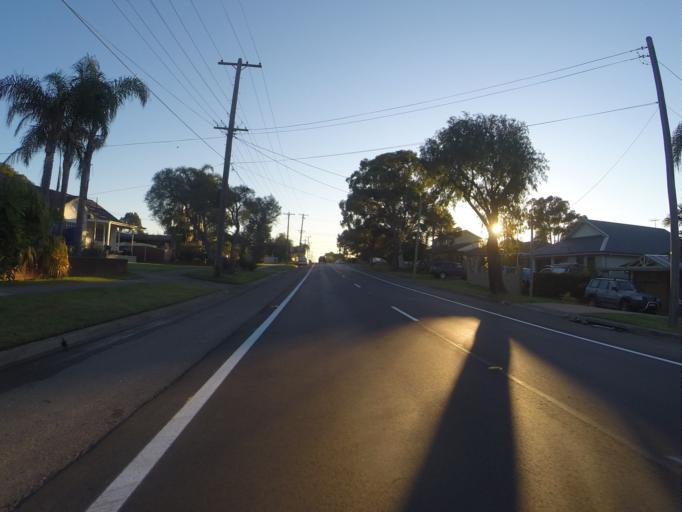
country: AU
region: New South Wales
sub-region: Sutherland Shire
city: Engadine
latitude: -34.0553
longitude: 151.0056
